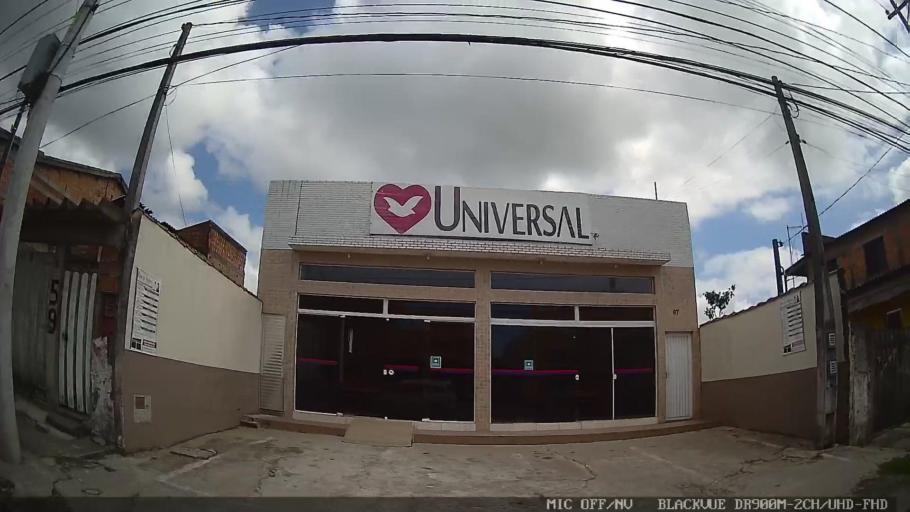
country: BR
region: Sao Paulo
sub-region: Peruibe
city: Peruibe
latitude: -24.2992
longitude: -47.0246
